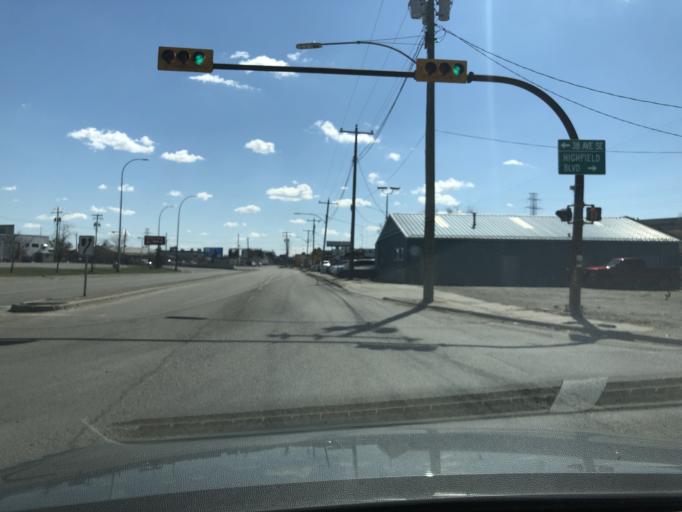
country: CA
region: Alberta
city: Calgary
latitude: 51.0201
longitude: -114.0301
